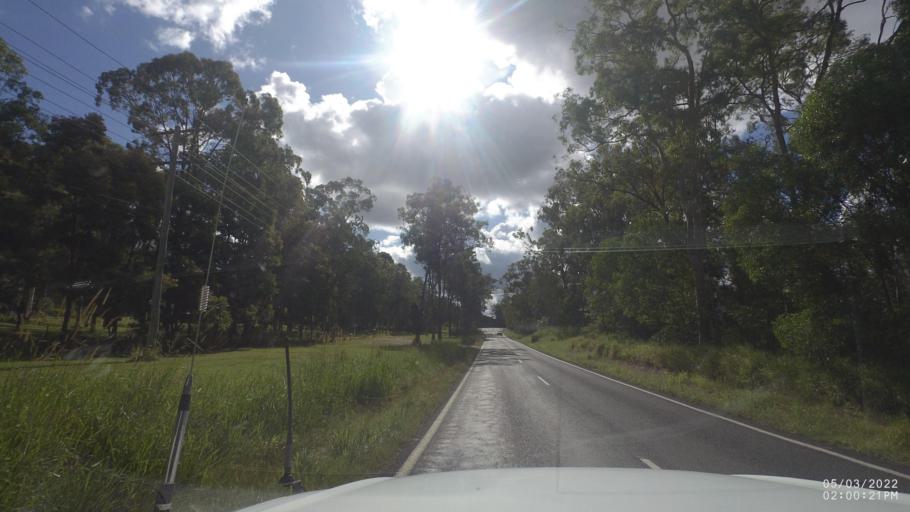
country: AU
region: Queensland
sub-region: Logan
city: Chambers Flat
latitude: -27.8240
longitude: 153.1025
